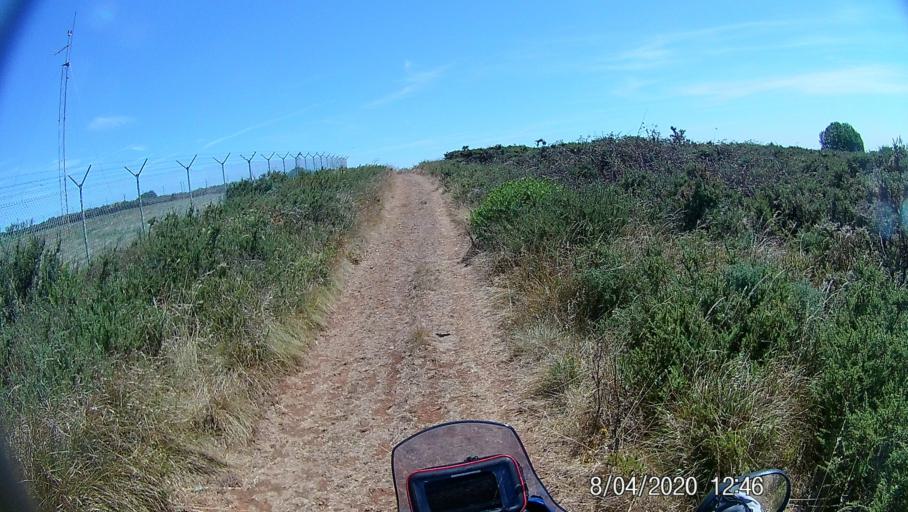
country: PT
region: Lisbon
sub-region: Sintra
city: Rio de Mouro
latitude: 38.7474
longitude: -9.3623
